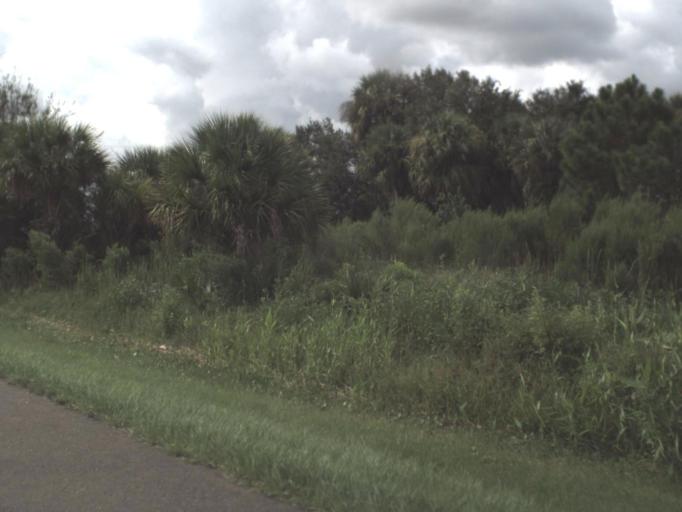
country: US
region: Florida
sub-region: Sarasota County
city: North Port
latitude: 27.1934
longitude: -82.0940
